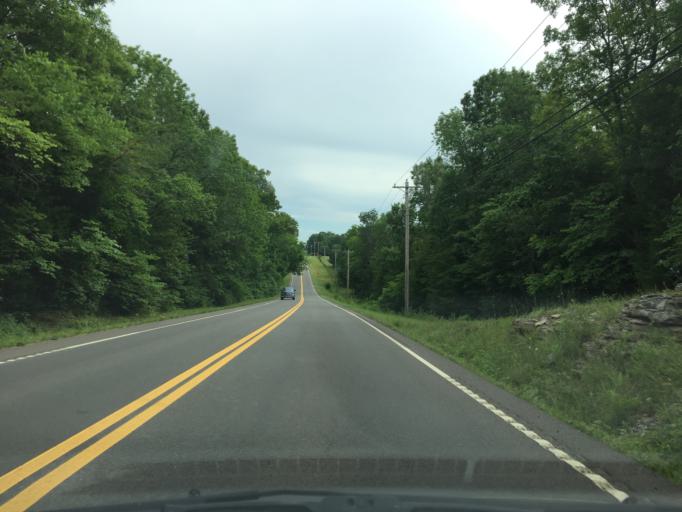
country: US
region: Tennessee
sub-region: Bradley County
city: Hopewell
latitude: 35.3183
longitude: -84.9444
